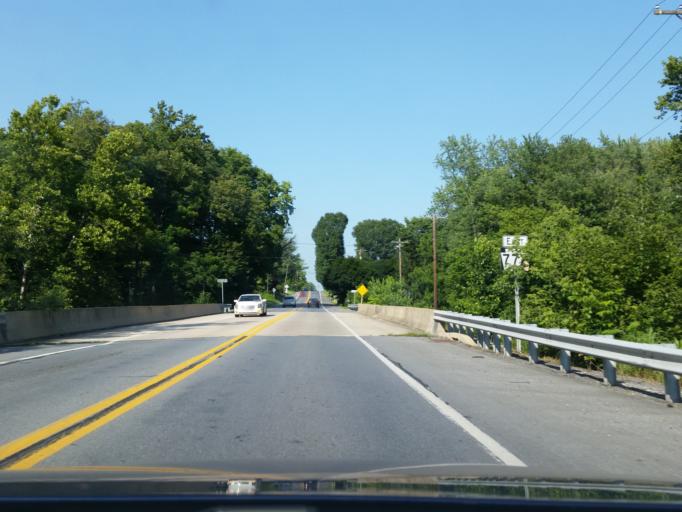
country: US
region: Pennsylvania
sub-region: Lancaster County
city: Mount Joy
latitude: 40.1159
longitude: -76.4997
